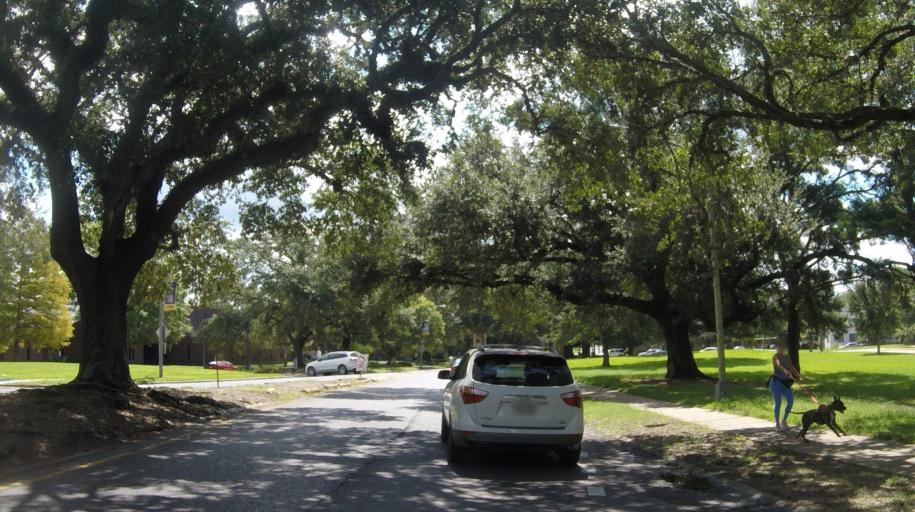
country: US
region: Louisiana
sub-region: East Baton Rouge Parish
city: Baton Rouge
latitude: 30.4054
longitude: -91.1749
